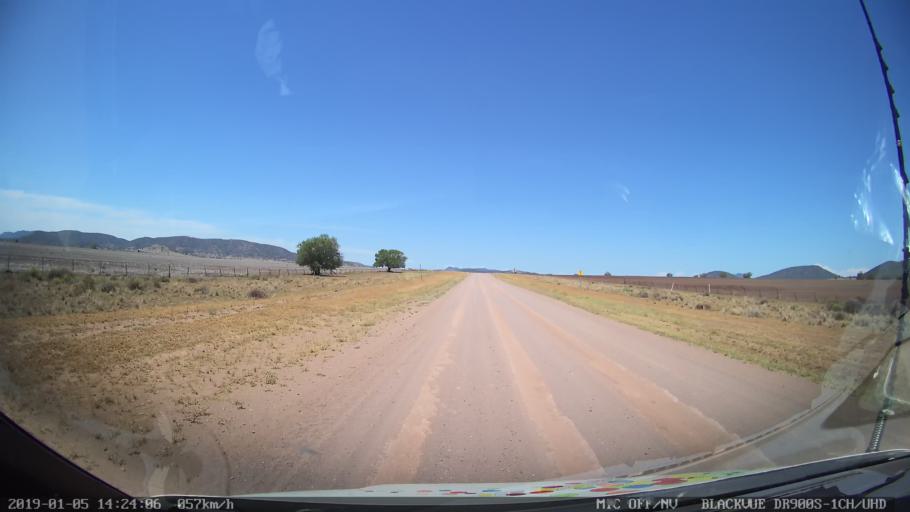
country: AU
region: New South Wales
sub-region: Liverpool Plains
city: Quirindi
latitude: -31.2417
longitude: 150.5365
